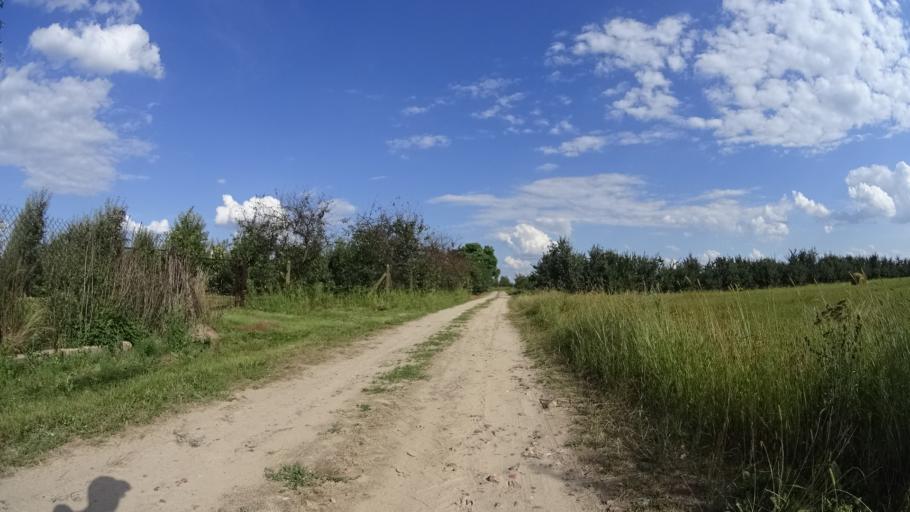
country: PL
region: Masovian Voivodeship
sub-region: Powiat bialobrzeski
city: Wysmierzyce
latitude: 51.6756
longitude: 20.7865
